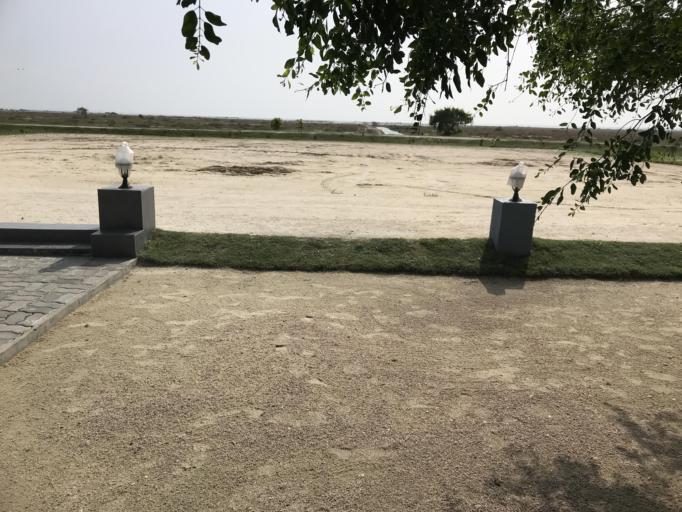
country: LK
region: Northern Province
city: Jaffna
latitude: 9.6715
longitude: 79.9251
